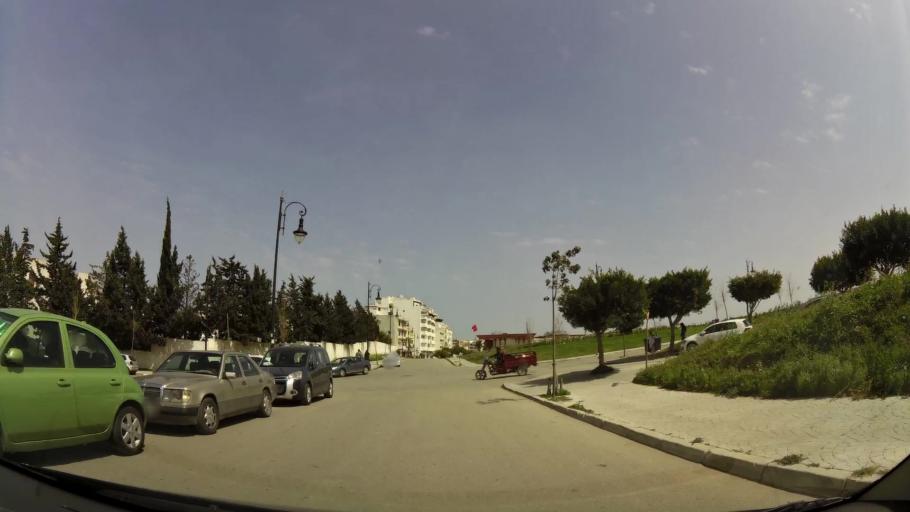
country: MA
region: Tanger-Tetouan
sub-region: Tanger-Assilah
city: Tangier
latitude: 35.7554
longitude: -5.8455
